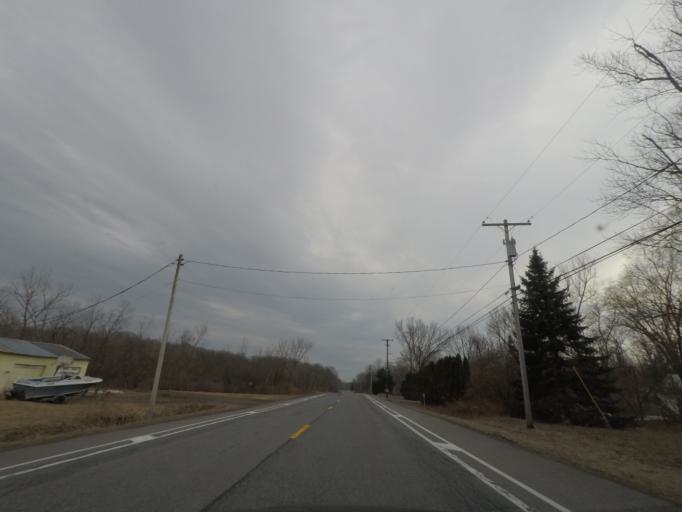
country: US
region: New York
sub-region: Washington County
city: Fort Edward
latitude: 43.1951
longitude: -73.5808
